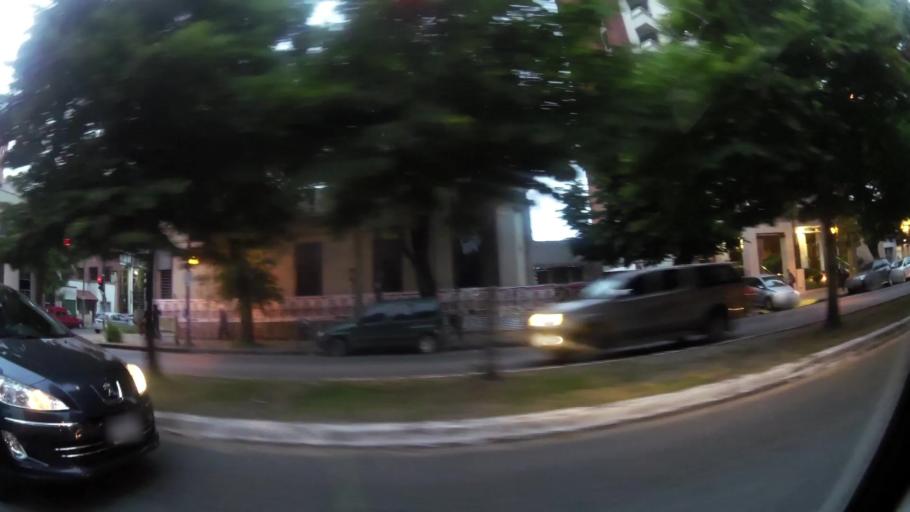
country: AR
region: Buenos Aires
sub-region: Partido de La Plata
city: La Plata
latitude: -34.9175
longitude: -57.9628
